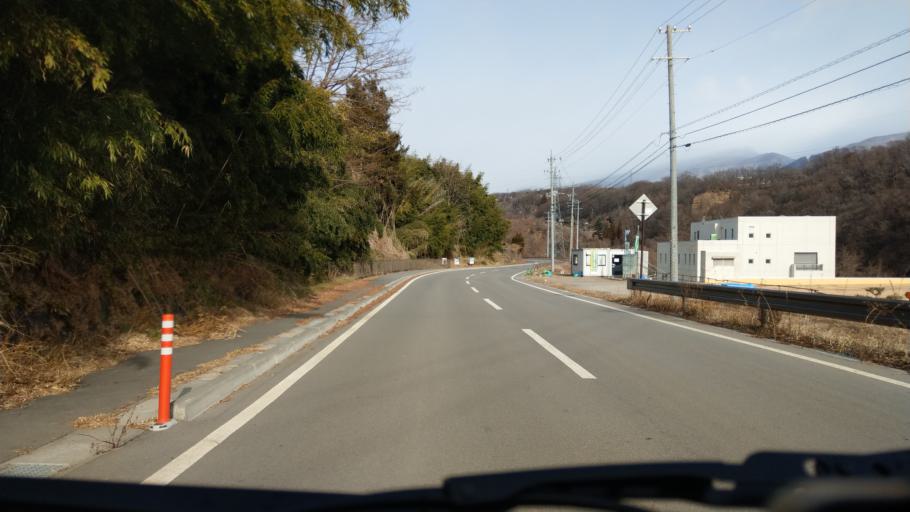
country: JP
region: Nagano
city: Komoro
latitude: 36.3296
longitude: 138.4042
